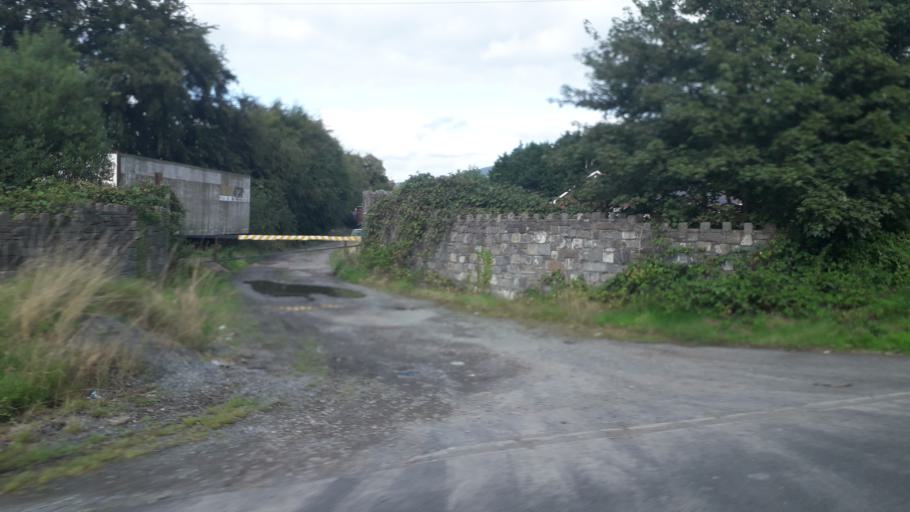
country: IE
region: Leinster
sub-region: Lu
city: Dundalk
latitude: 54.0344
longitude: -6.3769
